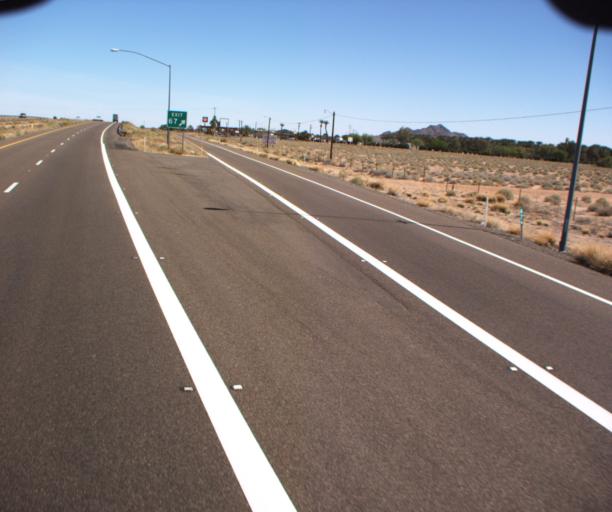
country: US
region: Arizona
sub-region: Yuma County
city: Wellton
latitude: 32.7988
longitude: -113.5450
